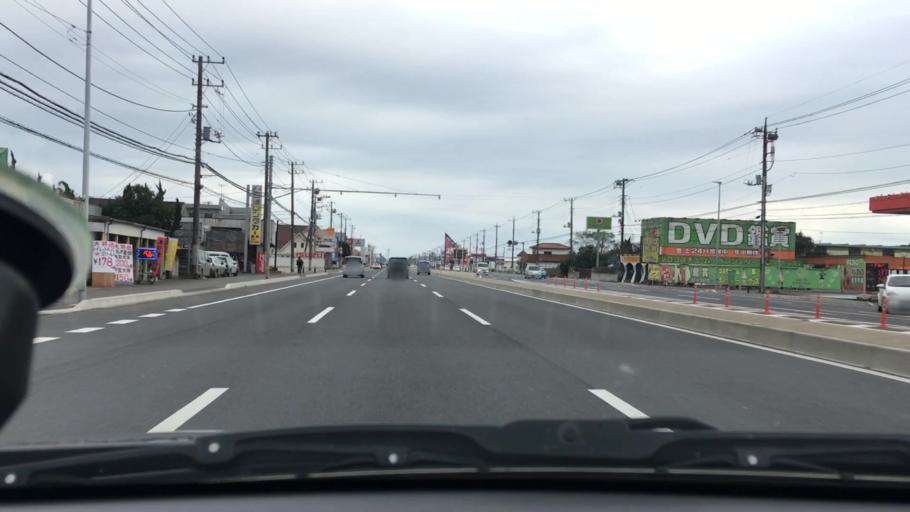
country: JP
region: Chiba
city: Omigawa
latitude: 35.8932
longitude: 140.6551
